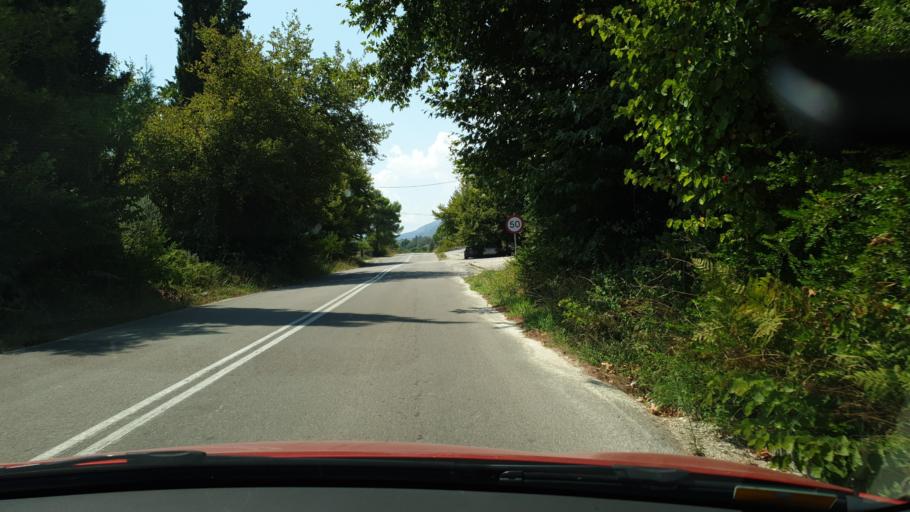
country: GR
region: Central Greece
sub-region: Nomos Evvoias
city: Oxilithos
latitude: 38.5951
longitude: 24.0750
